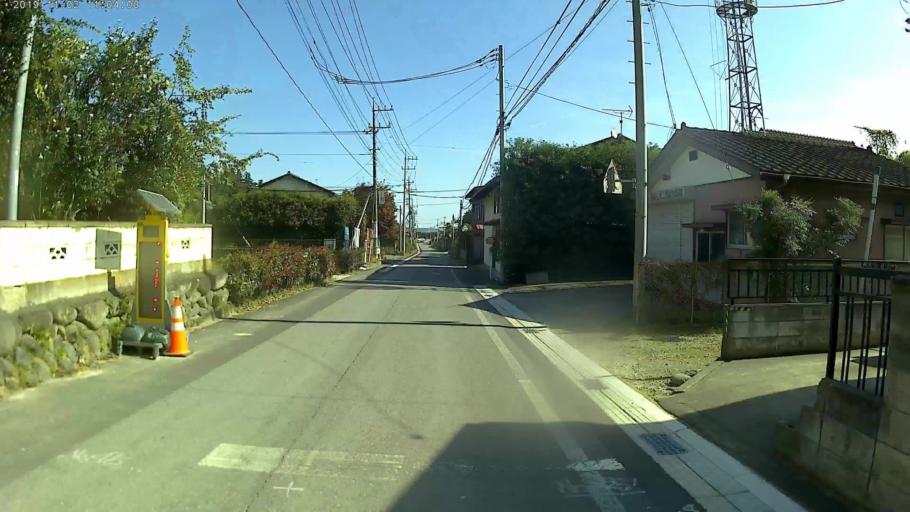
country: JP
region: Gunma
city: Annaka
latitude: 36.3063
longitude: 138.8325
